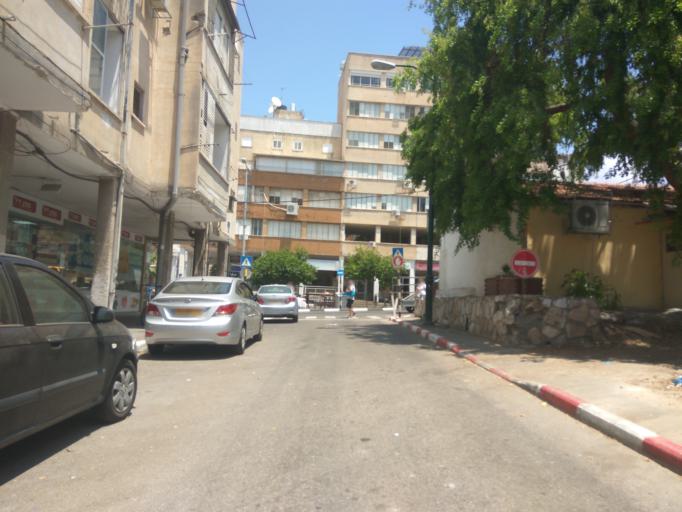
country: IL
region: Central District
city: Rishon LeZiyyon
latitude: 31.9639
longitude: 34.8062
